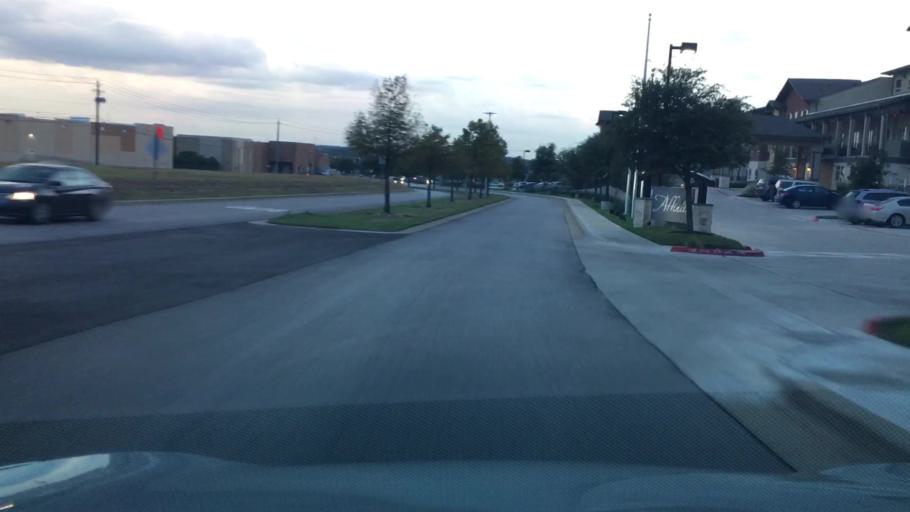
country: US
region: Texas
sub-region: Travis County
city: Onion Creek
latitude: 30.1645
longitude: -97.7950
